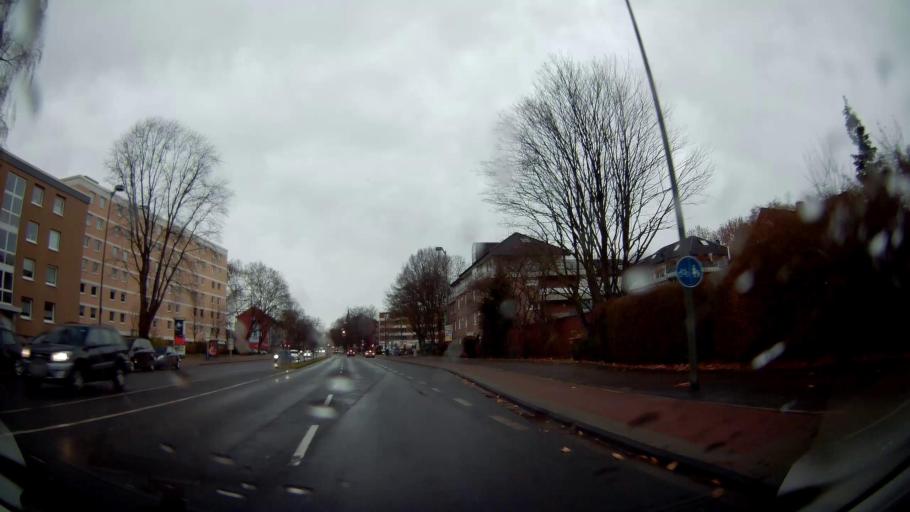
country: DE
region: North Rhine-Westphalia
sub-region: Regierungsbezirk Munster
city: Gelsenkirchen
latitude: 51.5069
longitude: 7.0778
